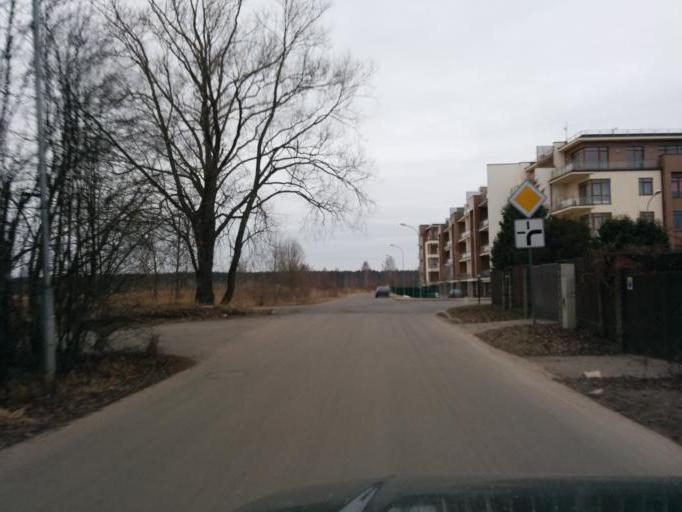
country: LV
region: Jurmala
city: Jurmala
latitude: 56.9624
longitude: 23.8191
